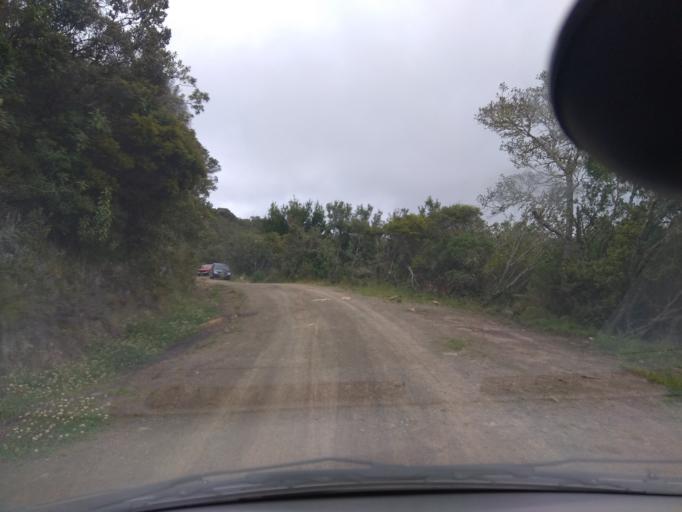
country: CO
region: Boyaca
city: Mongui
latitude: 5.7338
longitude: -72.8303
